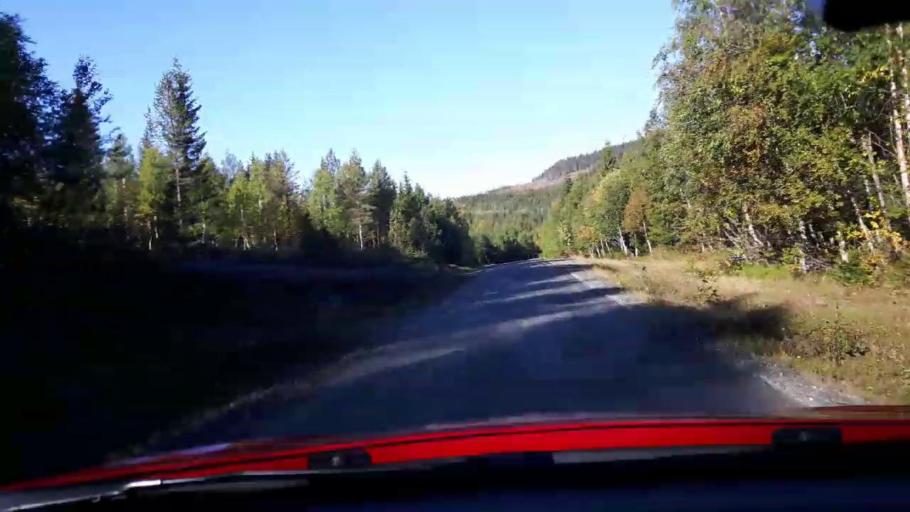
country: NO
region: Nord-Trondelag
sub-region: Lierne
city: Sandvika
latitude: 64.5880
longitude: 13.8653
